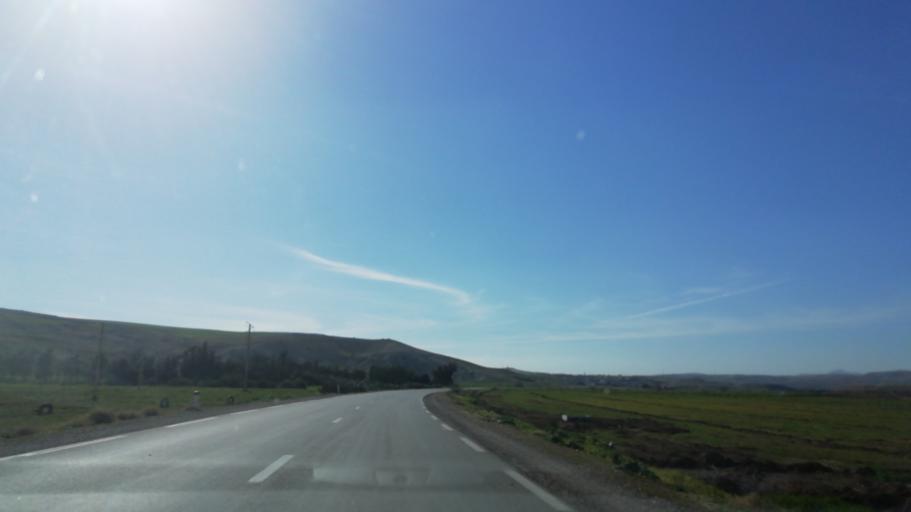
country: DZ
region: Mascara
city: Oued el Abtal
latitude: 35.4561
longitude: 0.7427
